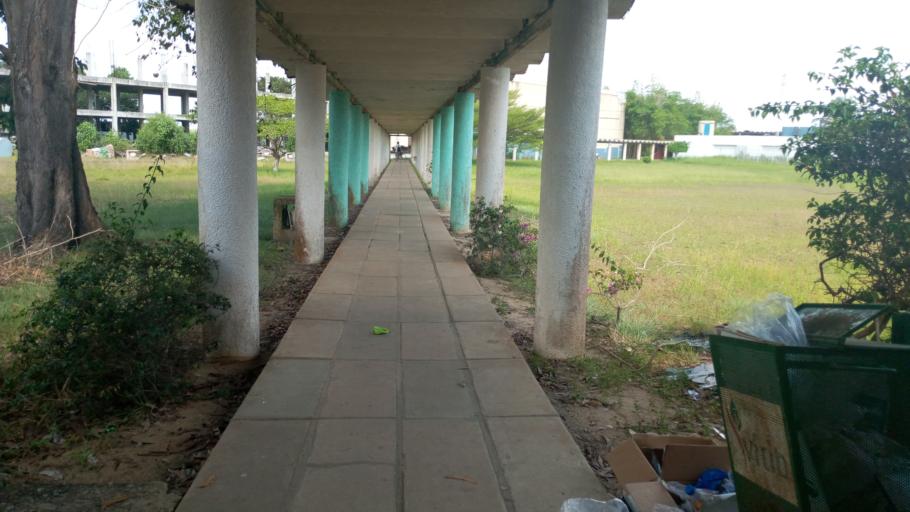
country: CI
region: Sud-Comoe
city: Grand-Bassam
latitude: 5.2298
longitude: -3.7592
